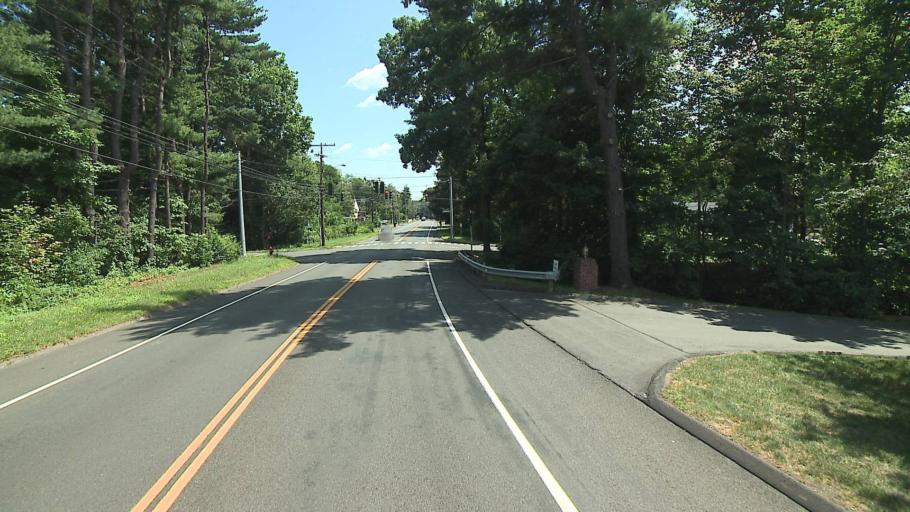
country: US
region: Connecticut
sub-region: Hartford County
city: Farmington
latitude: 41.7455
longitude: -72.8630
